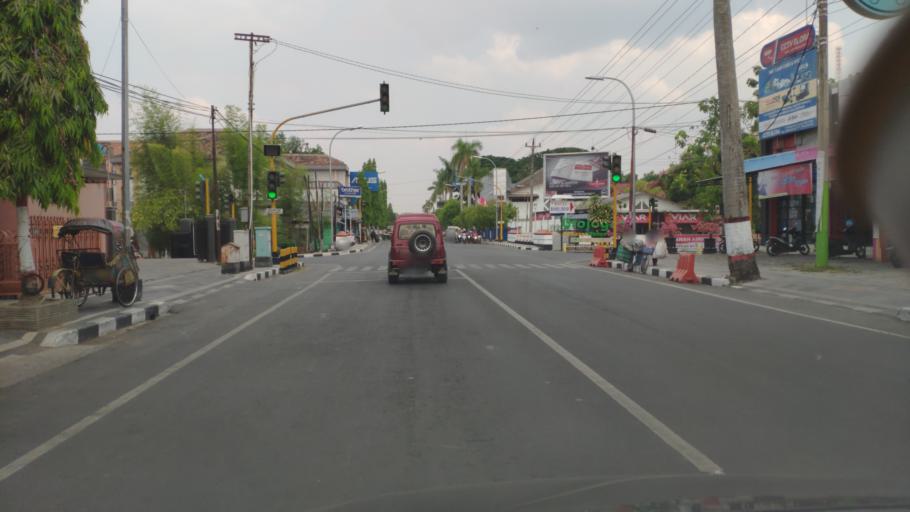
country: ID
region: Central Java
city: Blora
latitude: -6.9700
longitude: 111.4172
